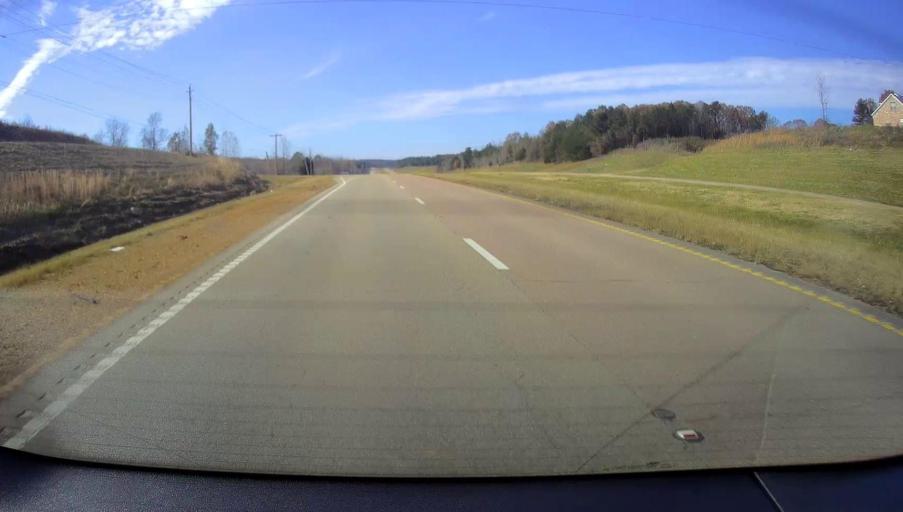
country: US
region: Mississippi
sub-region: Tippah County
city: Ripley
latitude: 34.9502
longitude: -88.9207
